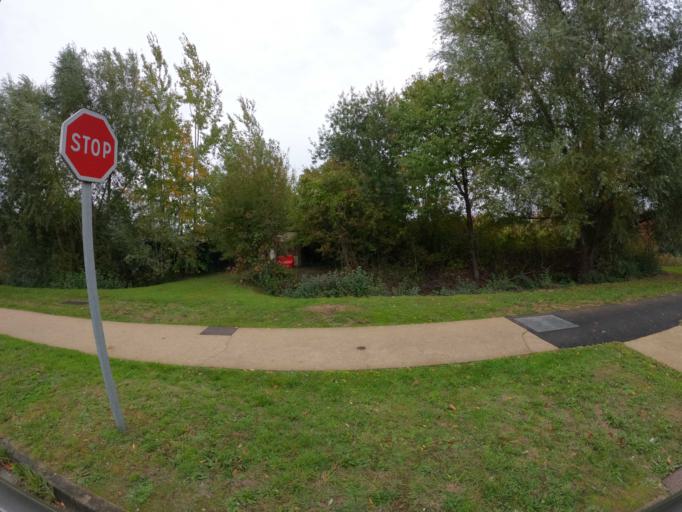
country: FR
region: Ile-de-France
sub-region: Departement de Seine-et-Marne
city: Serris
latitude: 48.8608
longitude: 2.7862
